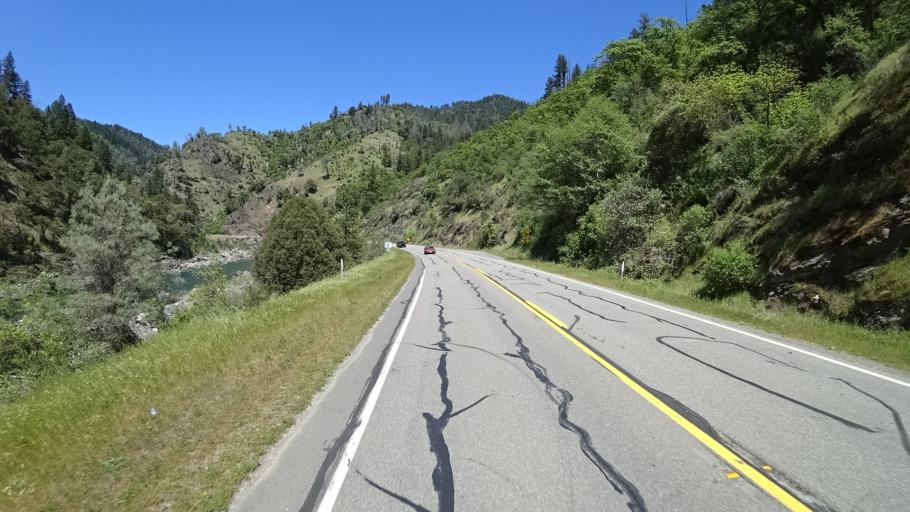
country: US
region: California
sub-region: Trinity County
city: Hayfork
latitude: 40.7578
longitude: -123.2821
